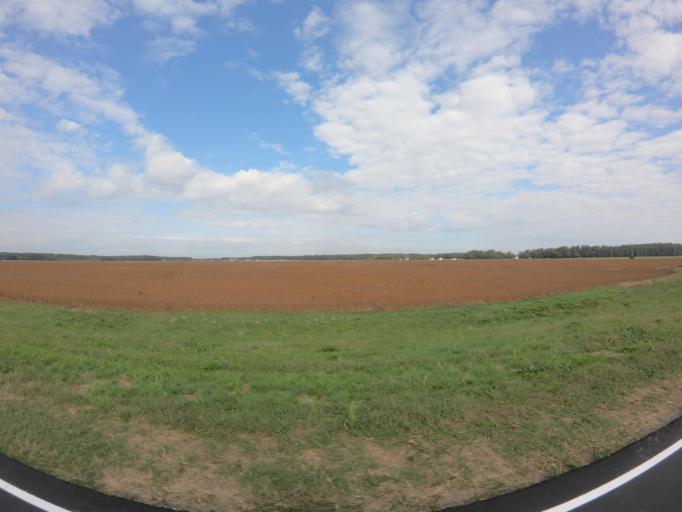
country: US
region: Delaware
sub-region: Sussex County
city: Bridgeville
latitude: 38.7625
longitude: -75.6135
